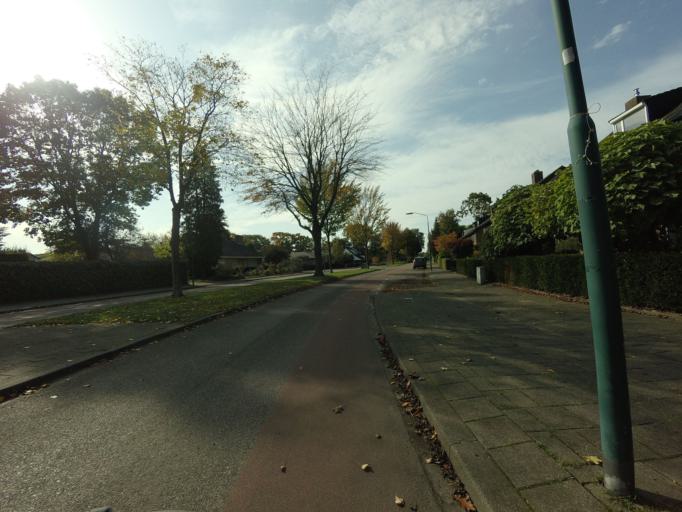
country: NL
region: North Brabant
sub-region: Gemeente Breda
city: Hoge Vucht
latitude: 51.6047
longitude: 4.8204
